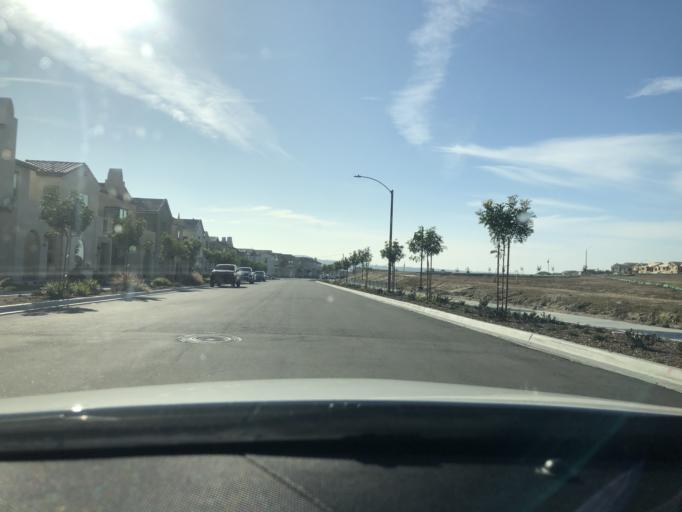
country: US
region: California
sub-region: San Diego County
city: Bonita
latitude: 32.5986
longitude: -116.9973
